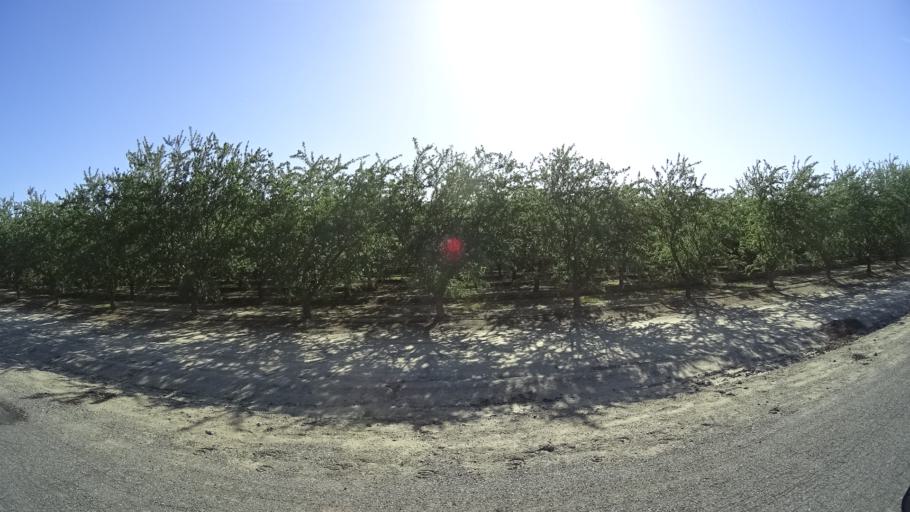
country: US
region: California
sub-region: Glenn County
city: Hamilton City
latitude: 39.7036
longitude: -122.0642
